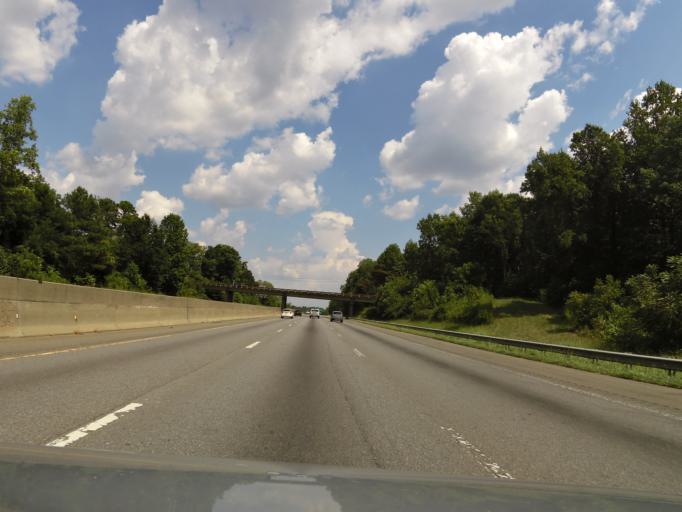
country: US
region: North Carolina
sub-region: Gaston County
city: Cramerton
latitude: 35.2641
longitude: -81.0704
